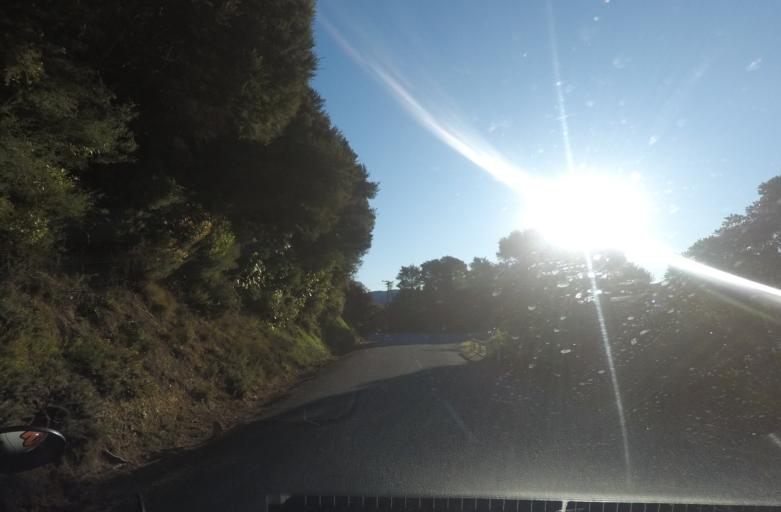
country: NZ
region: Marlborough
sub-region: Marlborough District
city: Picton
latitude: -41.2690
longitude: 173.9692
